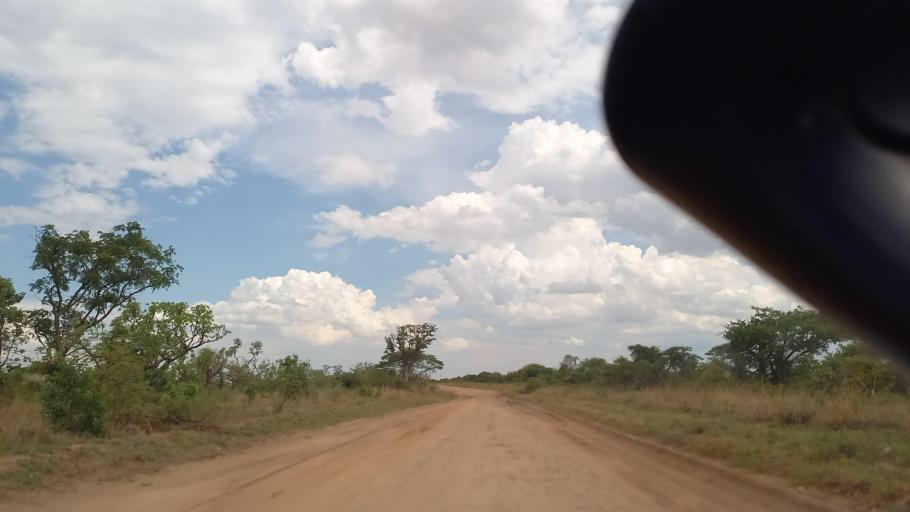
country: ZM
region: Southern
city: Nakambala
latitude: -16.0568
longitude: 27.9886
